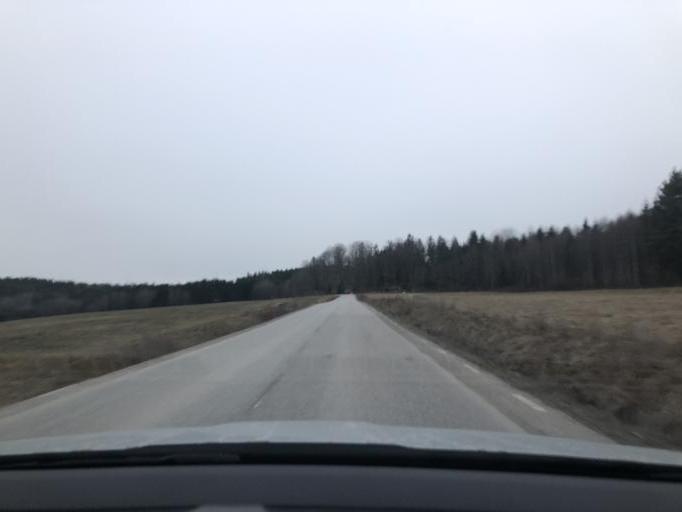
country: SE
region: Stockholm
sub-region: Botkyrka Kommun
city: Tullinge
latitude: 59.1673
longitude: 17.9024
